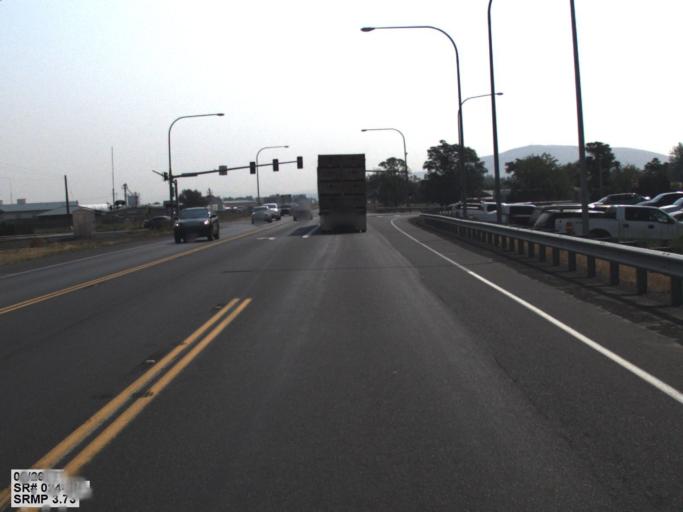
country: US
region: Washington
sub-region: Yakima County
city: Terrace Heights
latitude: 46.5628
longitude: -120.4052
